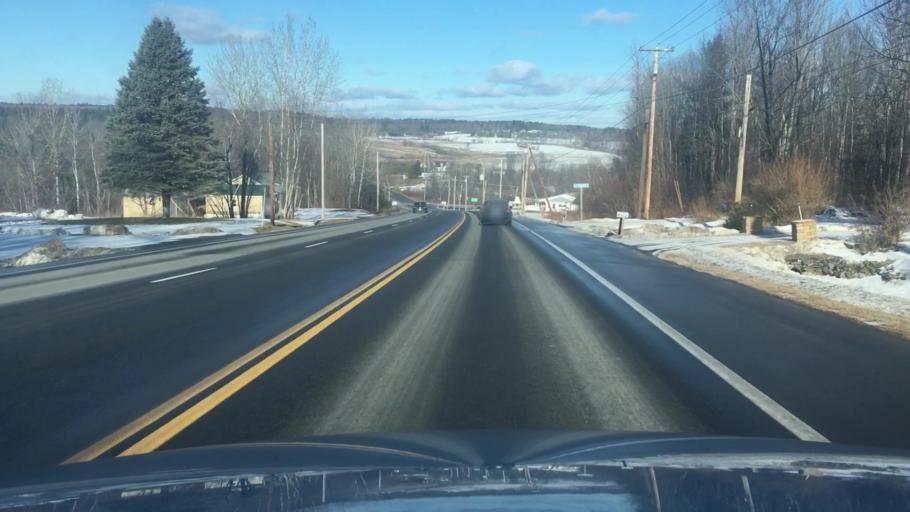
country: US
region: Maine
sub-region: Kennebec County
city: Waterville
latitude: 44.5952
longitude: -69.6539
